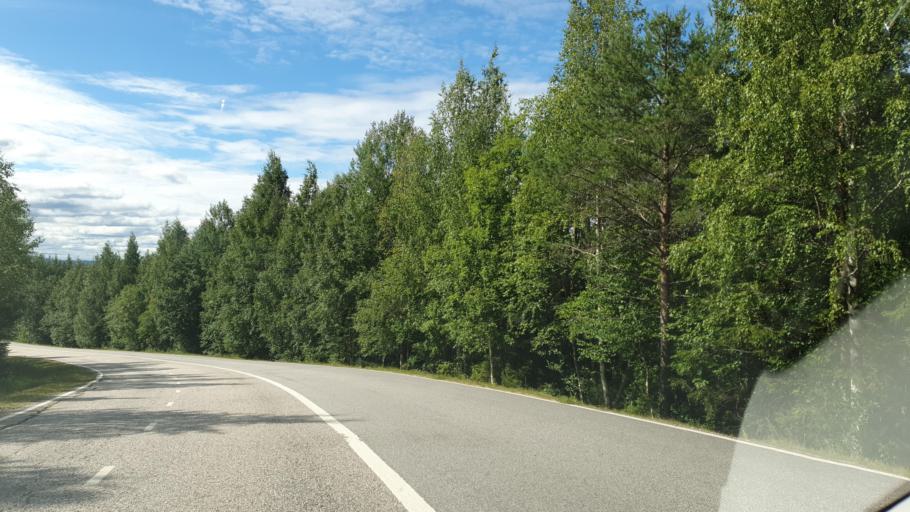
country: FI
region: Kainuu
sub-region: Kajaani
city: Vuokatti
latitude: 64.1307
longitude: 28.2497
